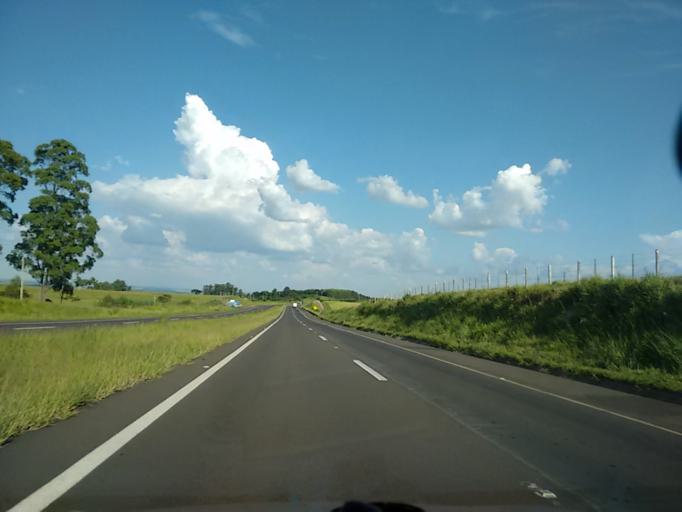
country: BR
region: Sao Paulo
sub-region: Garca
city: Garca
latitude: -22.2658
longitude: -49.5155
